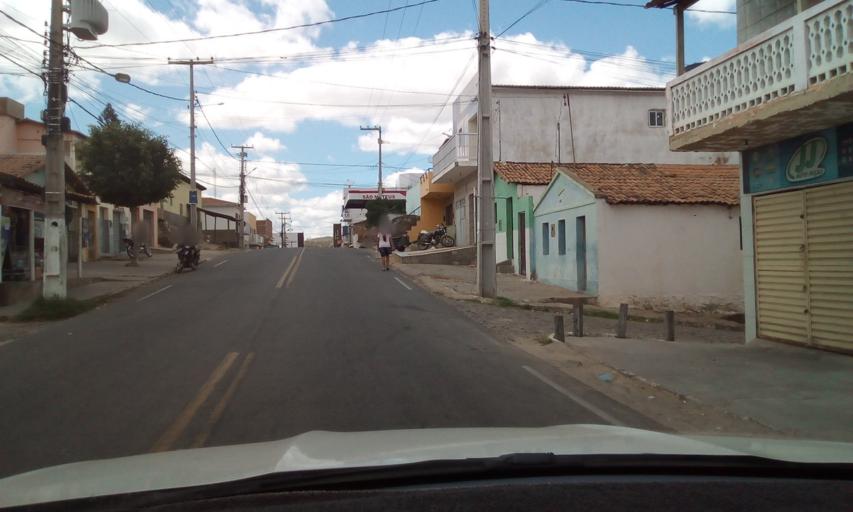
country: BR
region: Paraiba
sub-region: Picui
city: Picui
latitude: -6.5114
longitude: -36.3517
